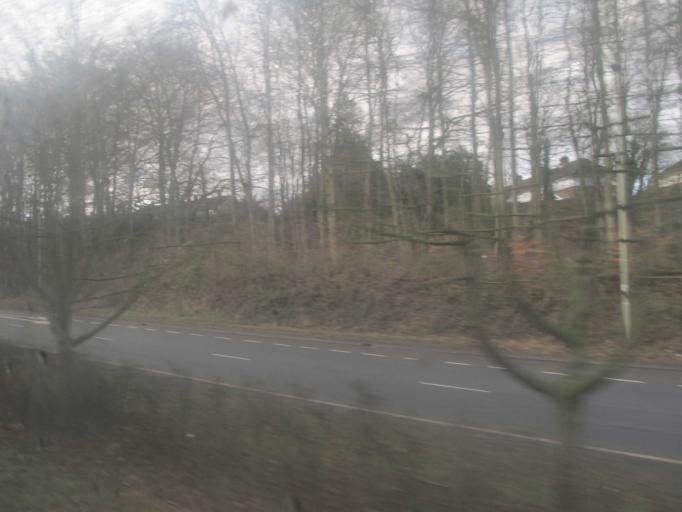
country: GB
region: England
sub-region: Hampshire
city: Basingstoke
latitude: 51.2605
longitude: -1.1060
